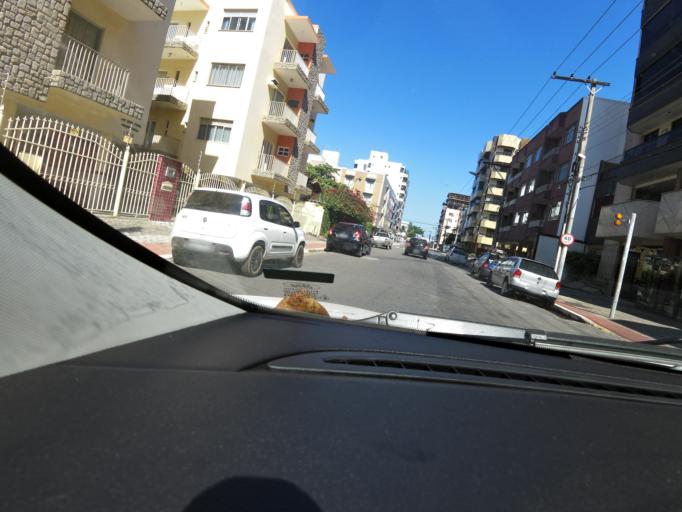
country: BR
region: Espirito Santo
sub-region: Guarapari
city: Guarapari
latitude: -20.6569
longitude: -40.4941
